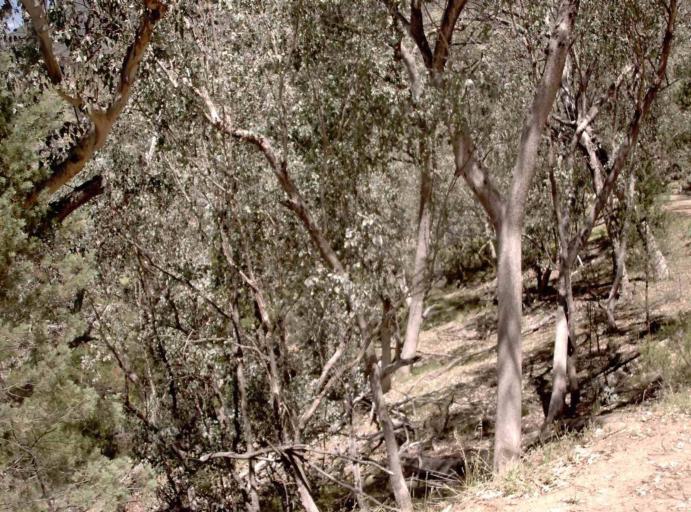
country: AU
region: New South Wales
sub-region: Snowy River
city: Jindabyne
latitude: -37.0909
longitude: 148.4361
